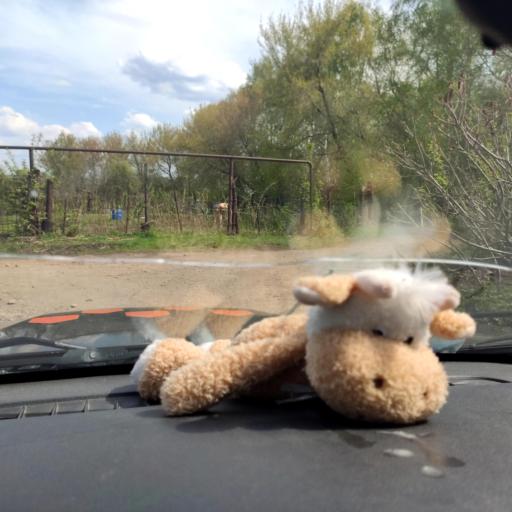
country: RU
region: Samara
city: Podstepki
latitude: 53.5107
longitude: 49.0836
